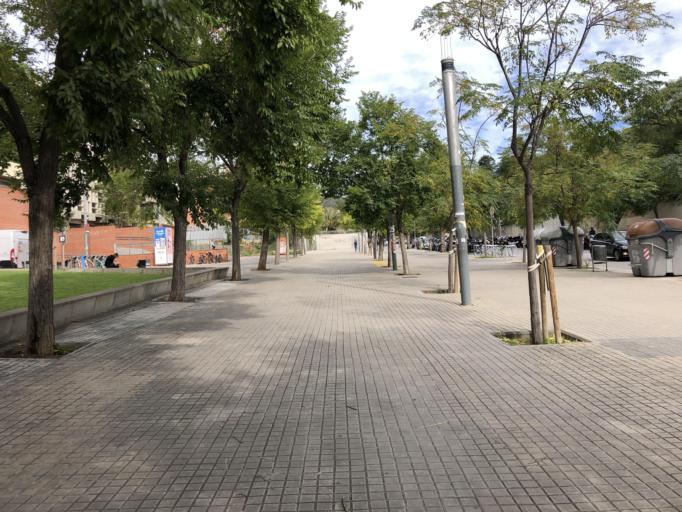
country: ES
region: Catalonia
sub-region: Provincia de Barcelona
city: les Corts
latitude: 41.3862
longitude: 2.1165
